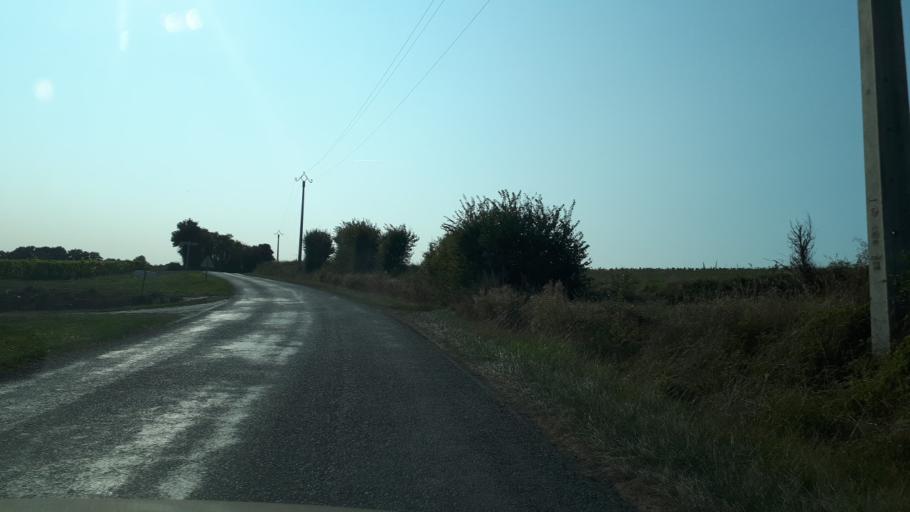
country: FR
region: Centre
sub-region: Departement du Cher
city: Menetou-Salon
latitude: 47.2315
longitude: 2.5124
